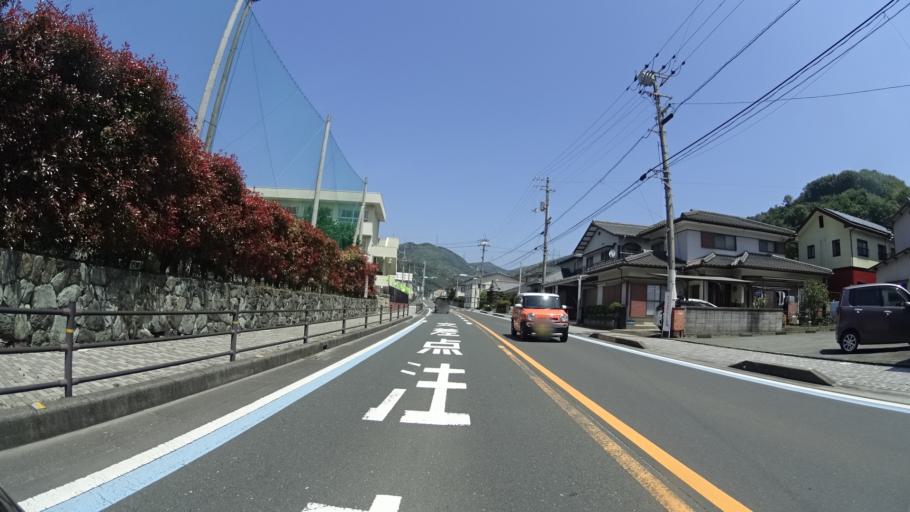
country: JP
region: Ehime
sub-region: Nishiuwa-gun
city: Ikata-cho
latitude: 33.4916
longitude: 132.3975
